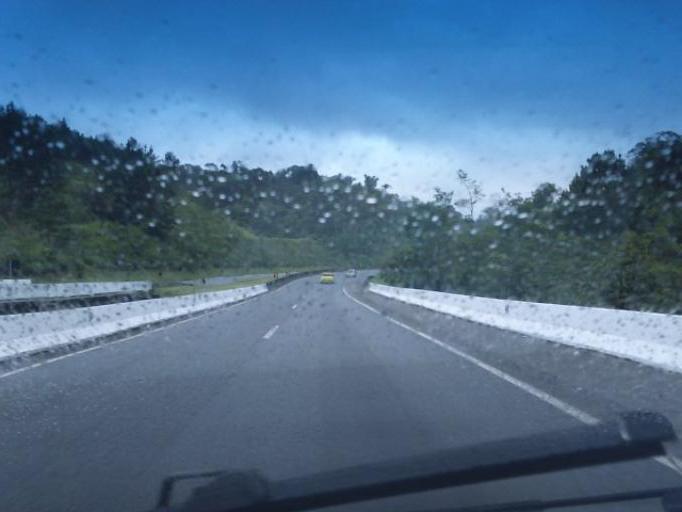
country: BR
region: Parana
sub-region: Antonina
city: Antonina
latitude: -25.0773
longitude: -48.5948
